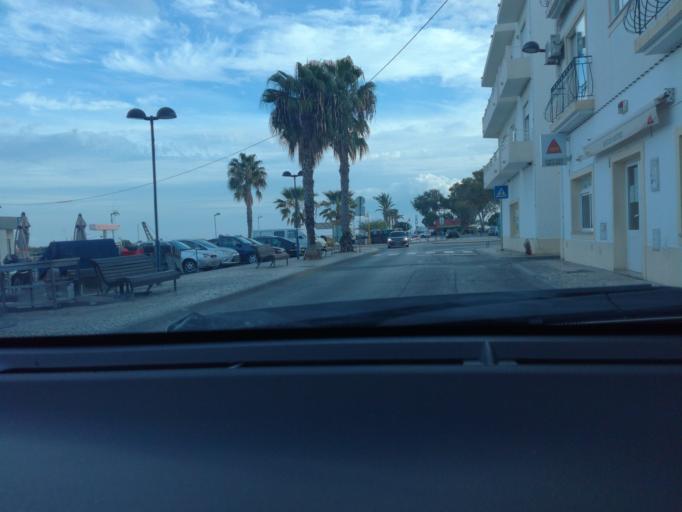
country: PT
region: Faro
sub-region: Olhao
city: Laranjeiro
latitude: 37.0554
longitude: -7.7446
